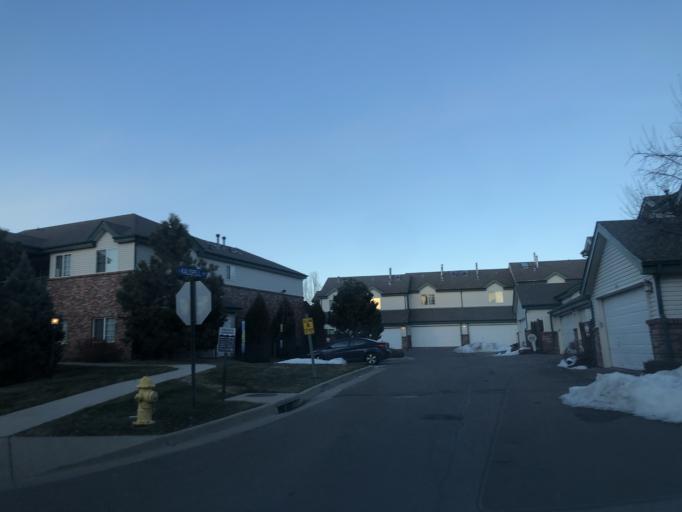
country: US
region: Colorado
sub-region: Adams County
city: Aurora
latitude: 39.7013
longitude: -104.8004
